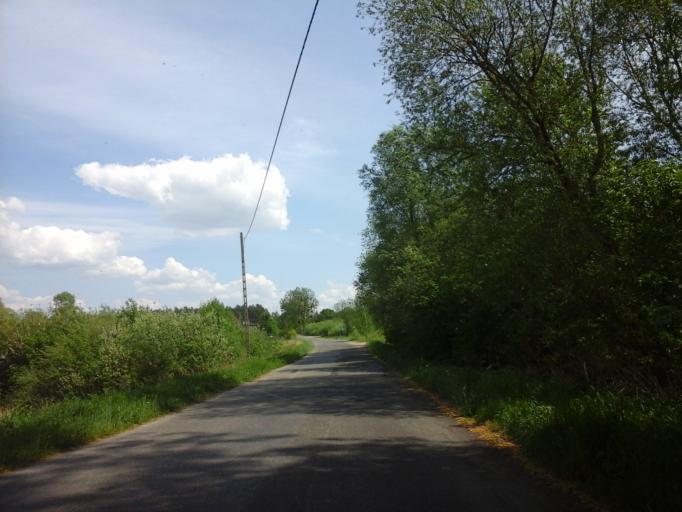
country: PL
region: West Pomeranian Voivodeship
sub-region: Powiat choszczenski
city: Choszczno
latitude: 53.1283
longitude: 15.4148
